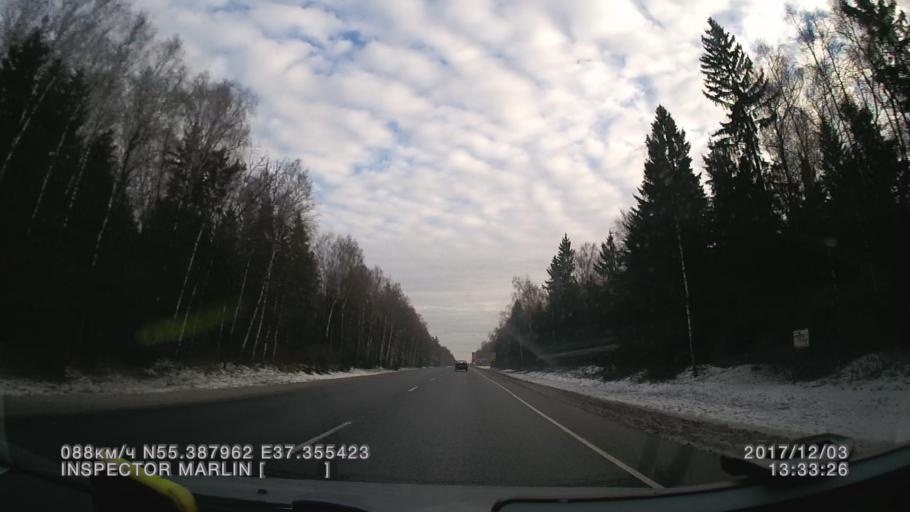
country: RU
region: Moskovskaya
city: Troitsk
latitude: 55.3879
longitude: 37.3556
